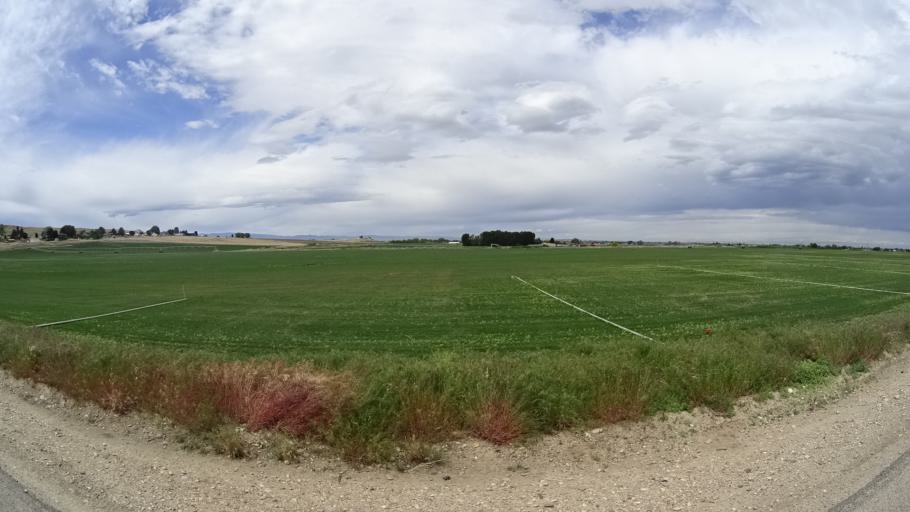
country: US
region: Idaho
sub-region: Ada County
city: Kuna
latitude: 43.4646
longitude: -116.4436
